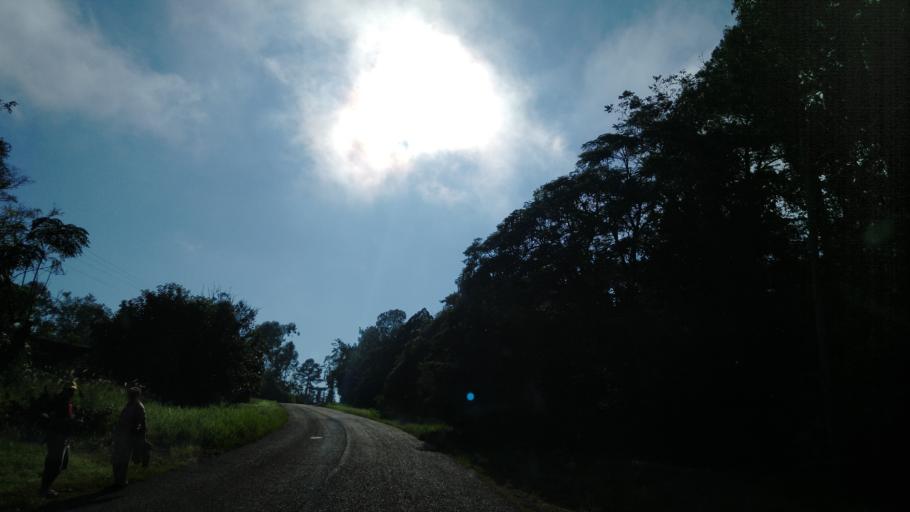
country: AR
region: Misiones
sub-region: Departamento de Montecarlo
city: Montecarlo
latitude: -26.5654
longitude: -54.7883
